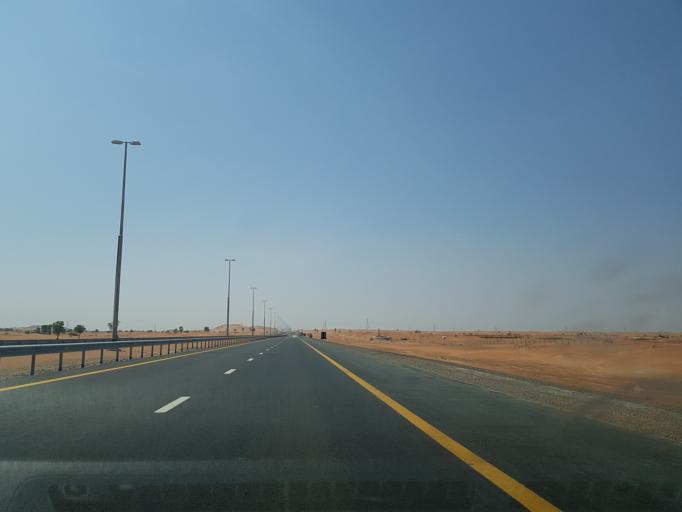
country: AE
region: Ash Shariqah
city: Adh Dhayd
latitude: 25.2419
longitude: 55.8751
